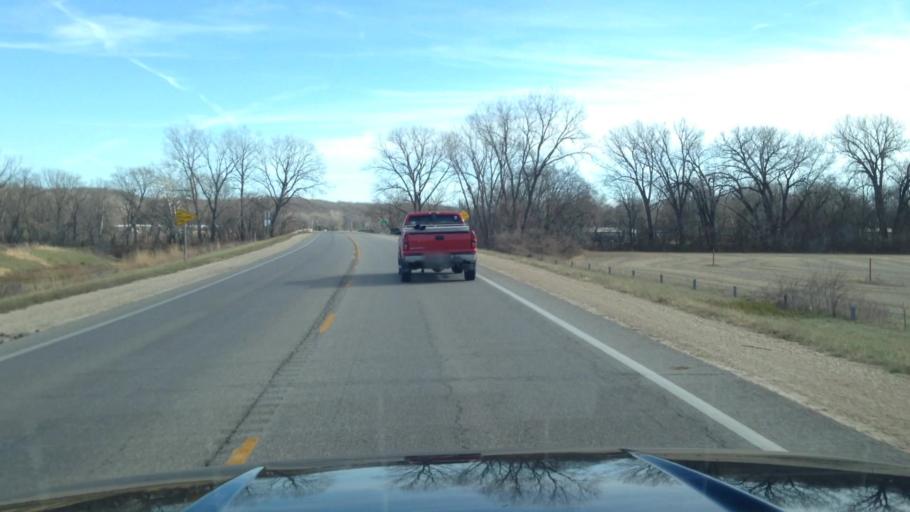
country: US
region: Kansas
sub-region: Jefferson County
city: Oskaloosa
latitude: 39.0807
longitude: -95.3997
